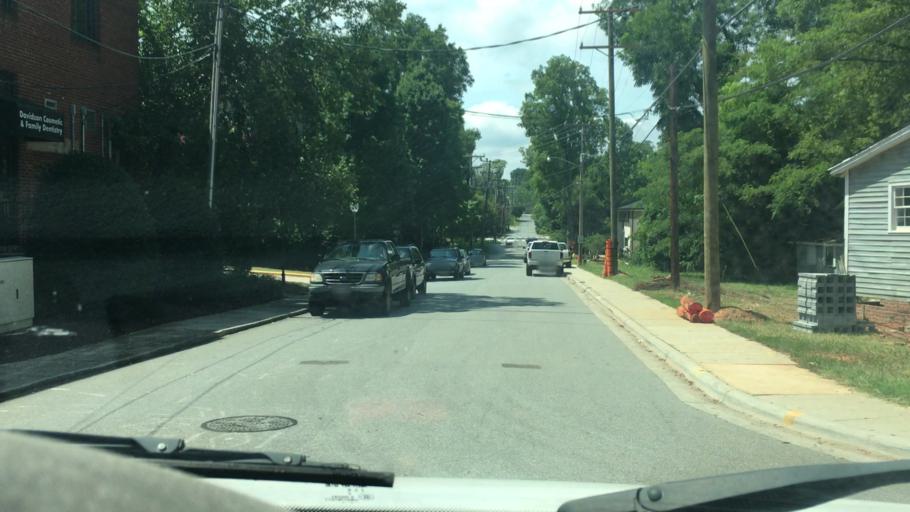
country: US
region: North Carolina
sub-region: Gaston County
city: Davidson
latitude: 35.5042
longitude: -80.8496
